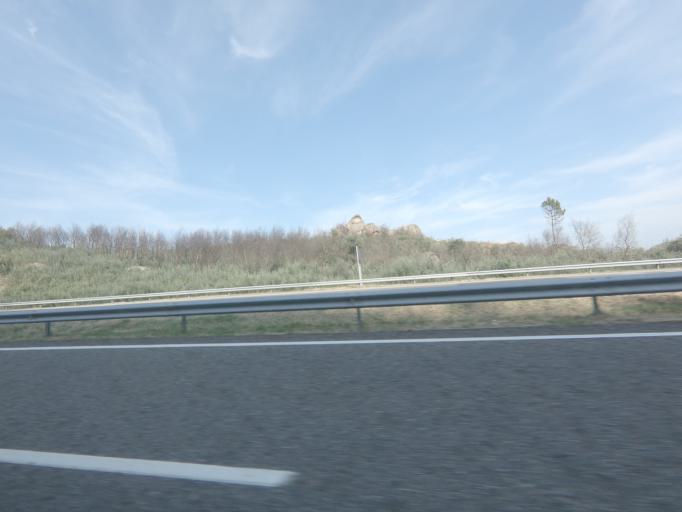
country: ES
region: Galicia
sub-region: Provincia de Ourense
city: Oimbra
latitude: 41.9343
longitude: -7.4996
